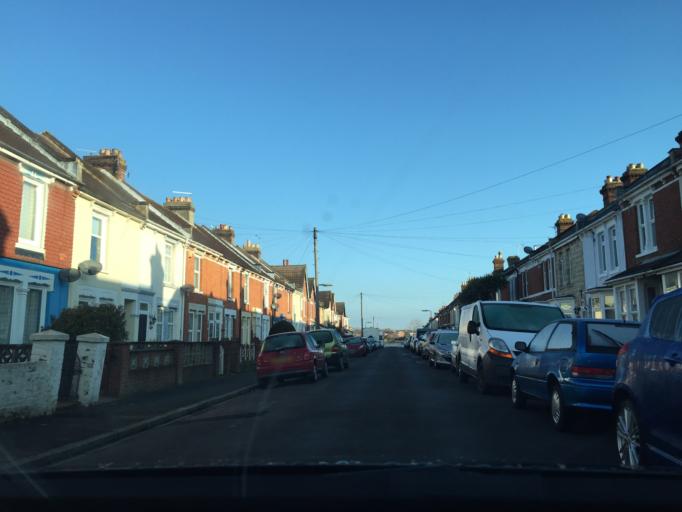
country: GB
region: England
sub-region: Hampshire
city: Gosport
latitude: 50.8013
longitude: -1.1330
